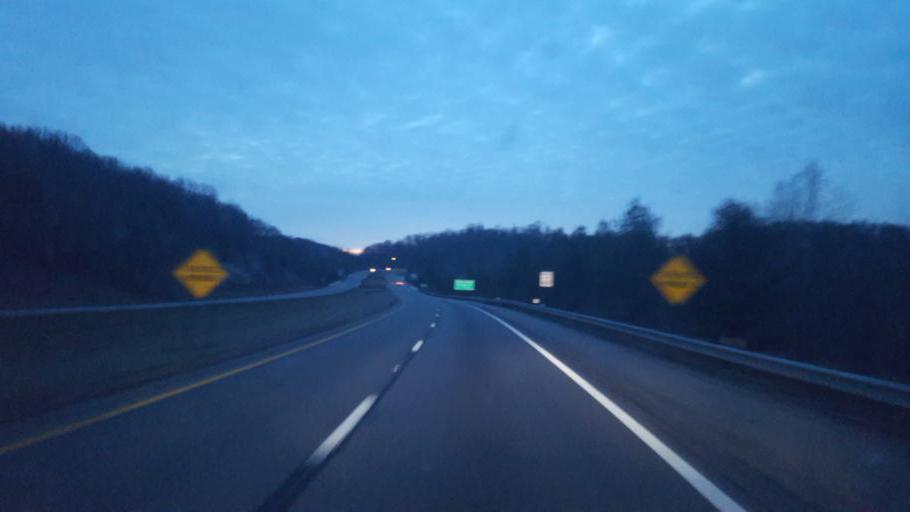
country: US
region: Ohio
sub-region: Jackson County
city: Jackson
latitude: 39.0648
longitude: -82.6249
